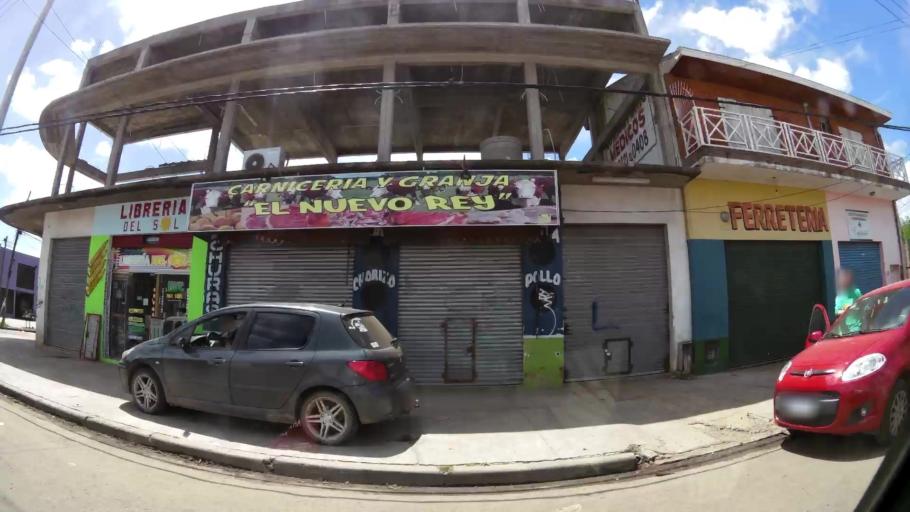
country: AR
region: Buenos Aires
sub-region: Partido de Quilmes
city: Quilmes
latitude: -34.8226
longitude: -58.2316
